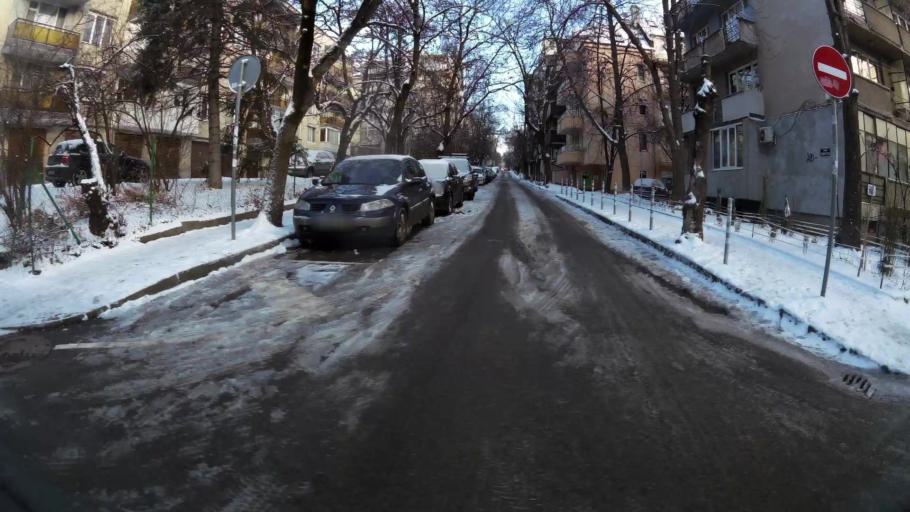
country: BG
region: Sofia-Capital
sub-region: Stolichna Obshtina
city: Sofia
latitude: 42.6697
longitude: 23.3237
